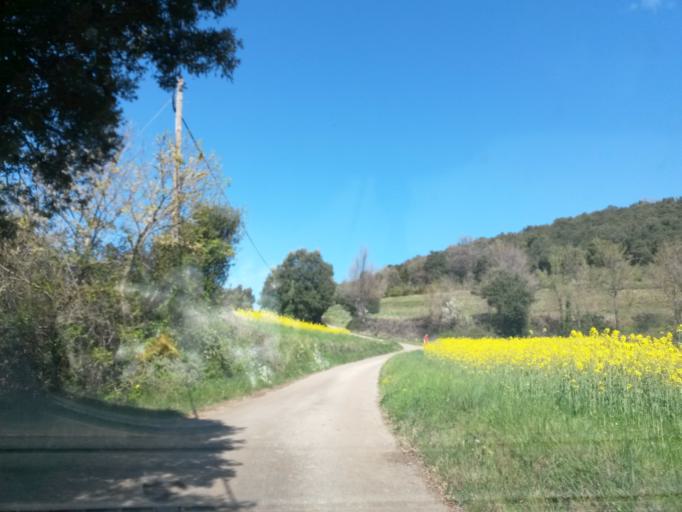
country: ES
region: Catalonia
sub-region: Provincia de Girona
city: Sant Cristofol de les Fonts
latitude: 42.1679
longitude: 2.5356
